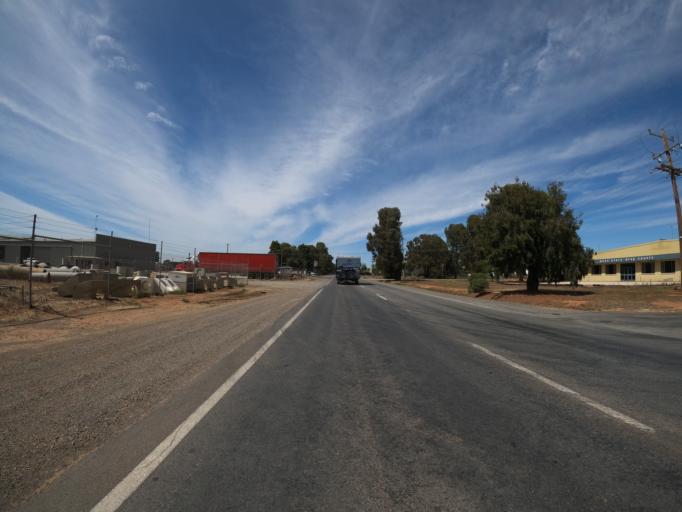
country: AU
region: Victoria
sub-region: Moira
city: Yarrawonga
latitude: -36.0298
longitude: 145.9955
